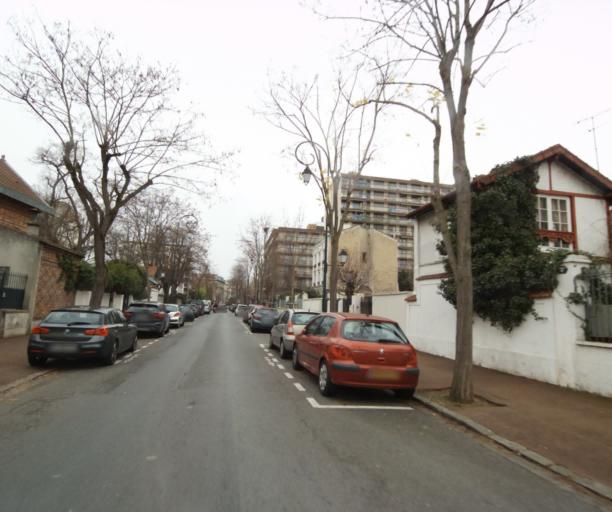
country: FR
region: Ile-de-France
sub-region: Departement des Yvelines
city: Chatou
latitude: 48.8847
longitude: 2.1733
